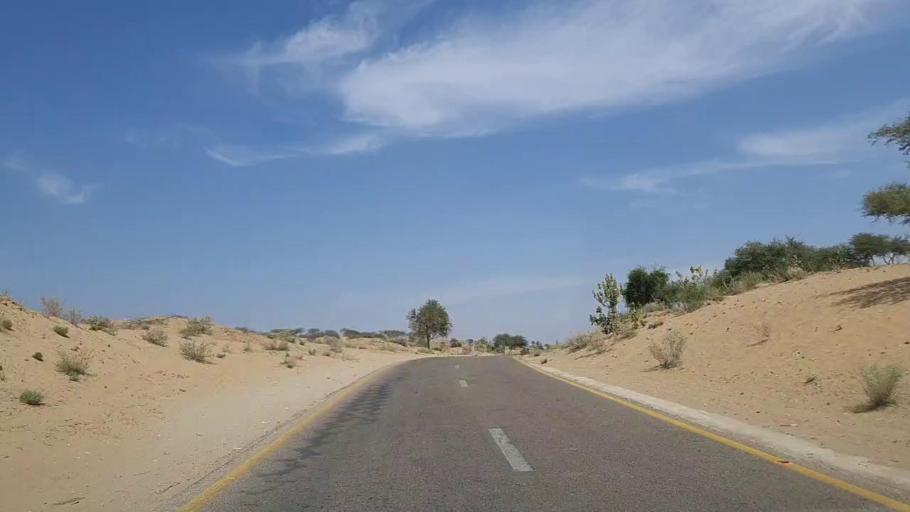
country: PK
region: Sindh
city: Mithi
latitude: 24.8075
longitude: 69.8155
